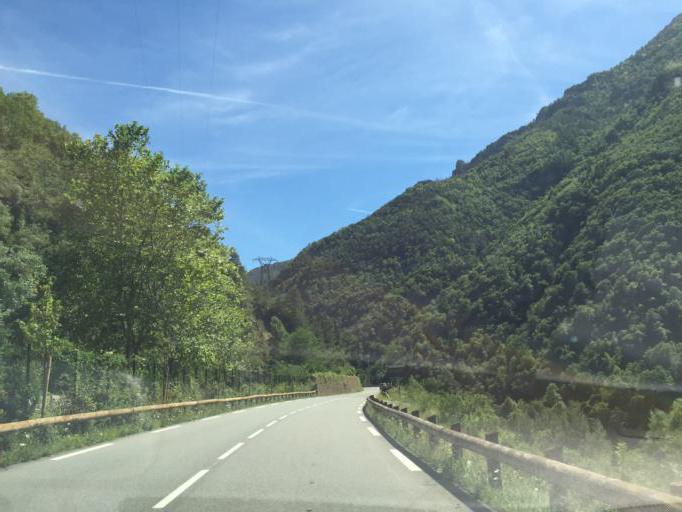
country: FR
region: Provence-Alpes-Cote d'Azur
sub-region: Departement des Alpes-Maritimes
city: Saint-Martin-Vesubie
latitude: 44.0731
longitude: 7.1096
